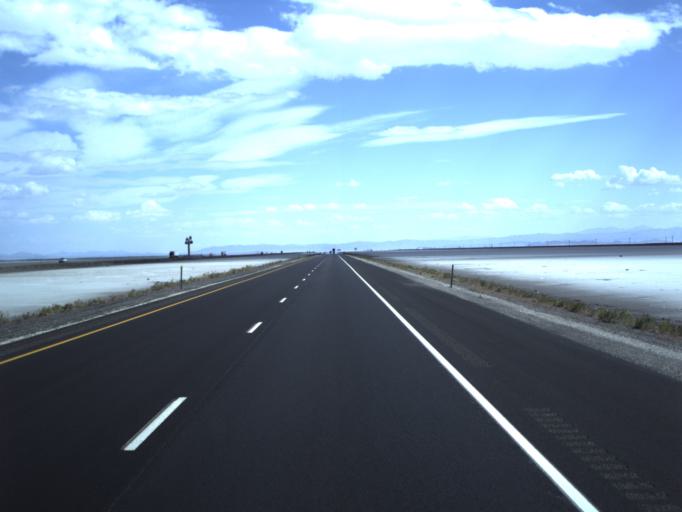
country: US
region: Utah
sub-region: Tooele County
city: Wendover
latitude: 40.7324
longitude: -113.5641
